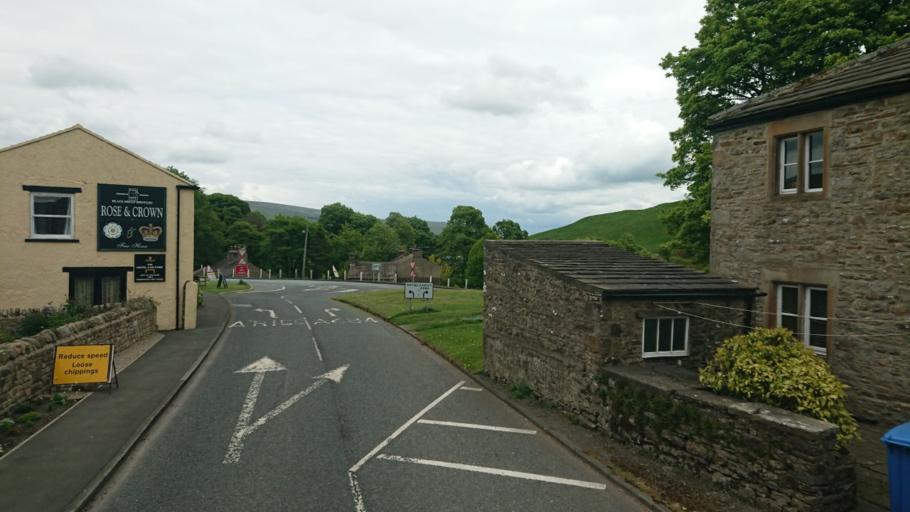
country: GB
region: England
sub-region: County Durham
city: Bowes
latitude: 54.3084
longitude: -2.1037
